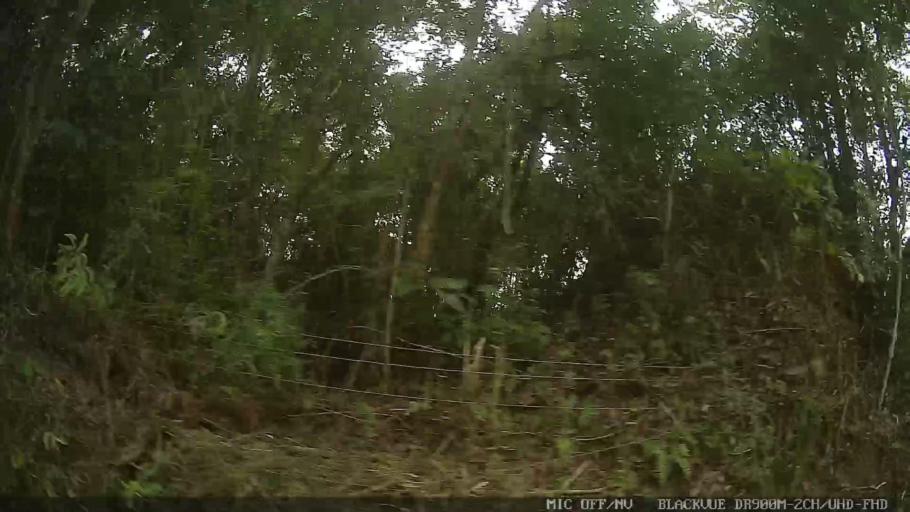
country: BR
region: Sao Paulo
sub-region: Mogi das Cruzes
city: Mogi das Cruzes
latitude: -23.4772
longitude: -46.2296
